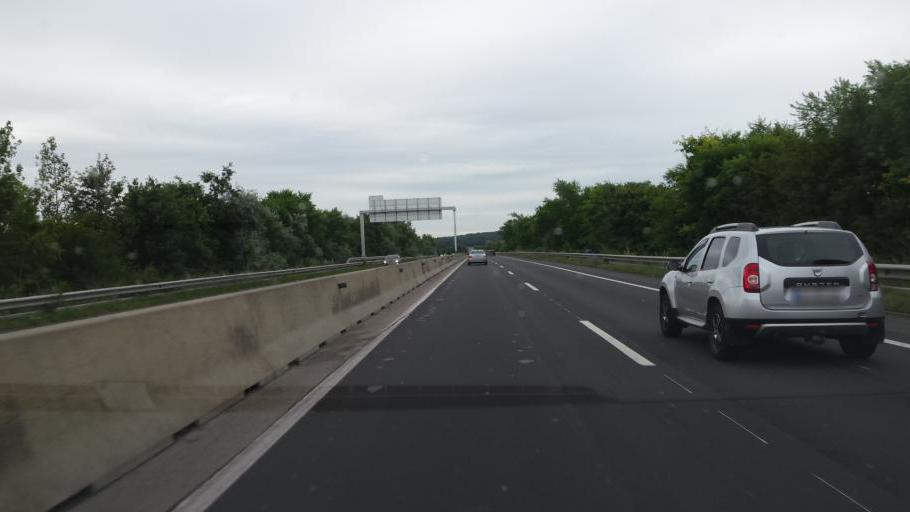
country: AT
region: Lower Austria
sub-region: Politischer Bezirk Wien-Umgebung
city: Fischamend Dorf
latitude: 48.1068
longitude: 16.6419
